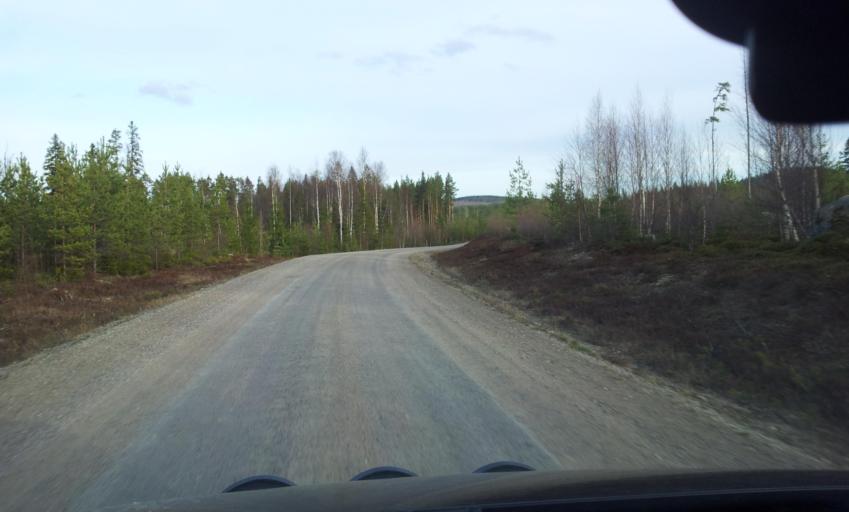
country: SE
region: Gaevleborg
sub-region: Ljusdals Kommun
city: Farila
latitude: 62.1265
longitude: 15.6690
